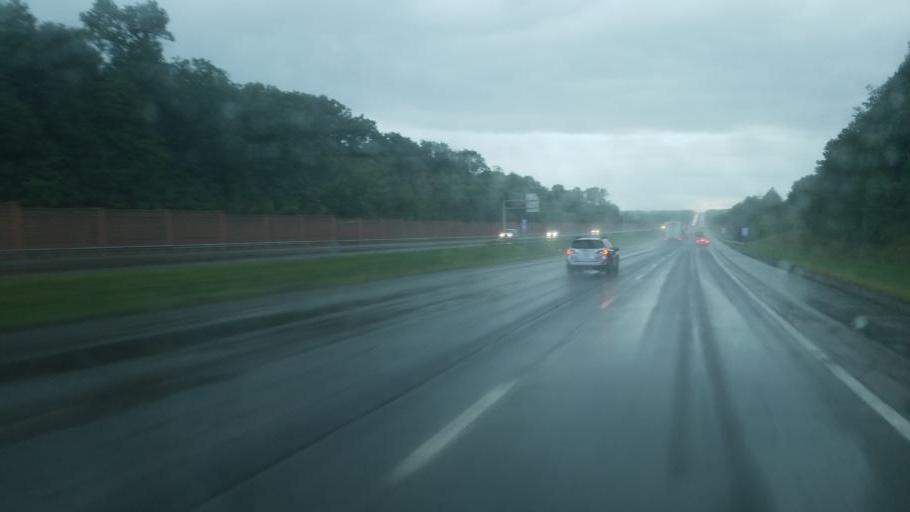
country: US
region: Ohio
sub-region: Medina County
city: Medina
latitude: 41.1290
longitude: -81.7987
